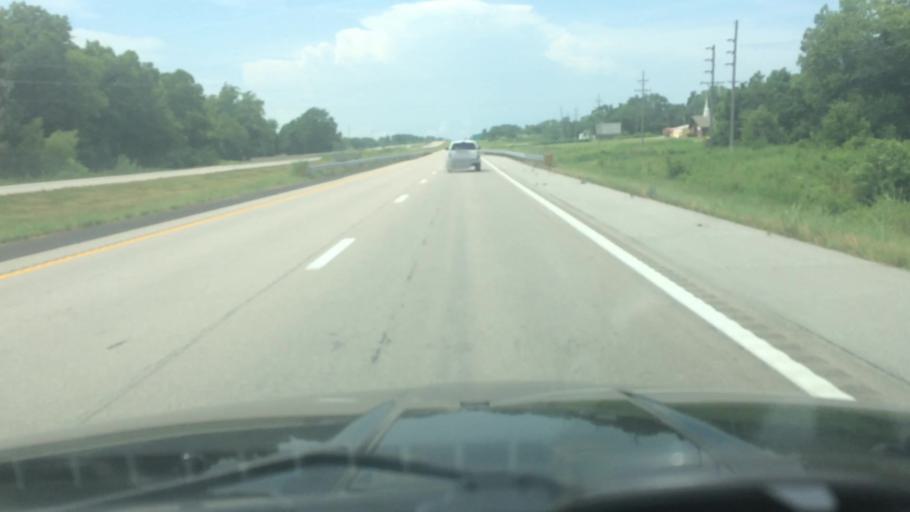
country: US
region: Missouri
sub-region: Polk County
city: Humansville
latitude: 37.7867
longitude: -93.5811
